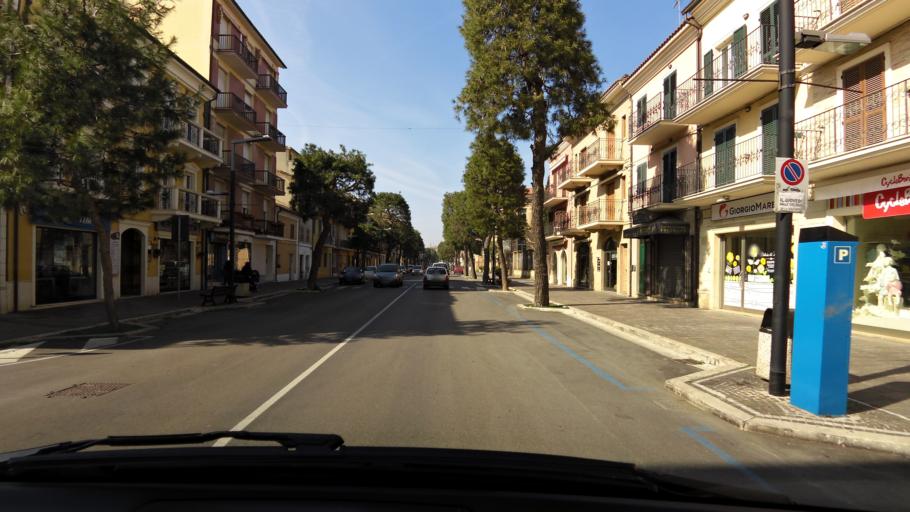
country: IT
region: The Marches
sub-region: Provincia di Macerata
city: Porto Recanati
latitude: 43.4308
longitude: 13.6646
